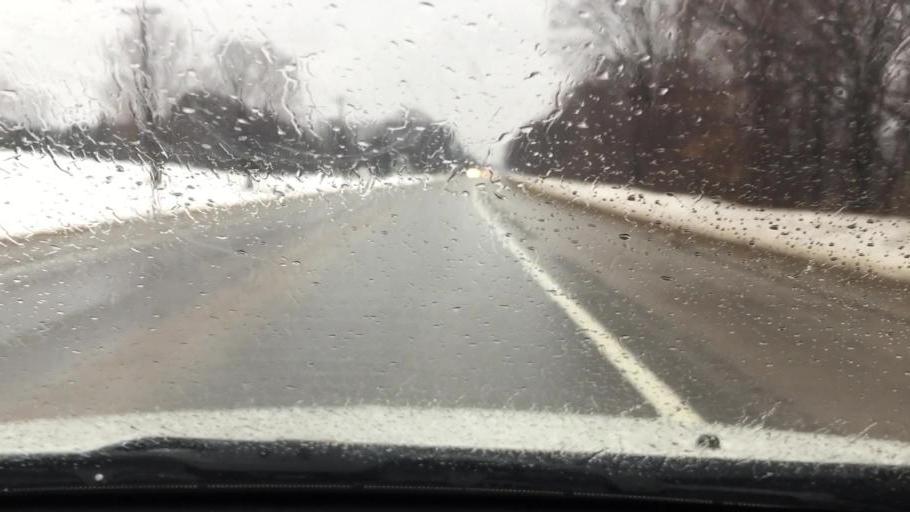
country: US
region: Michigan
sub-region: Charlevoix County
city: Charlevoix
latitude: 45.2839
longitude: -85.2404
